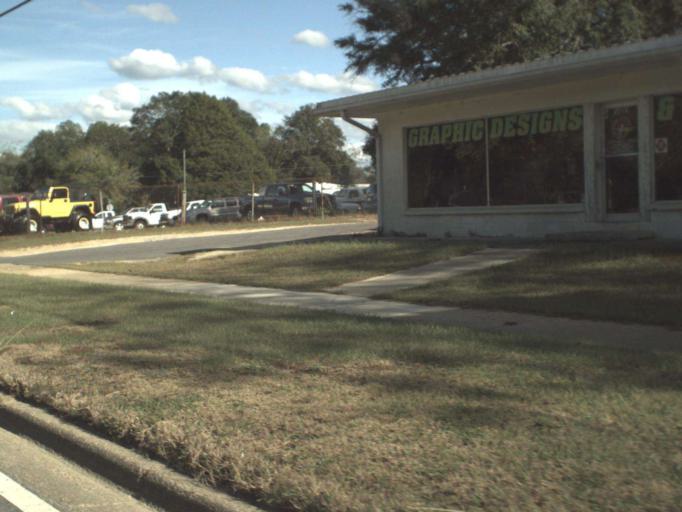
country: US
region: Florida
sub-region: Washington County
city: Chipley
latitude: 30.7779
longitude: -85.5498
